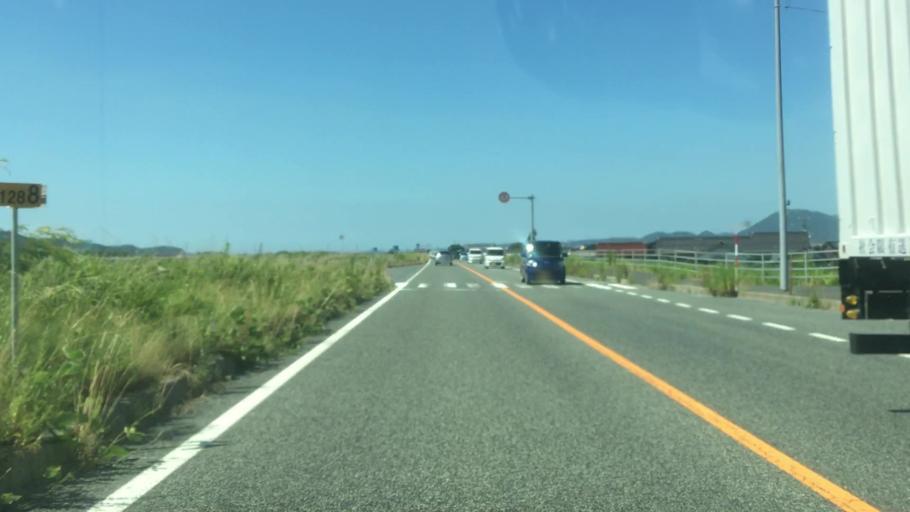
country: JP
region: Tottori
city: Tottori
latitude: 35.4560
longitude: 134.2152
